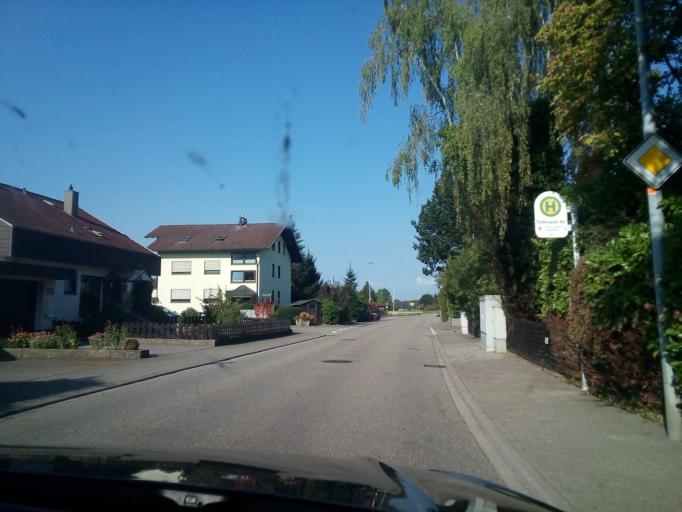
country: DE
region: Baden-Wuerttemberg
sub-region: Karlsruhe Region
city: Sinzheim
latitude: 48.7716
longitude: 8.1617
